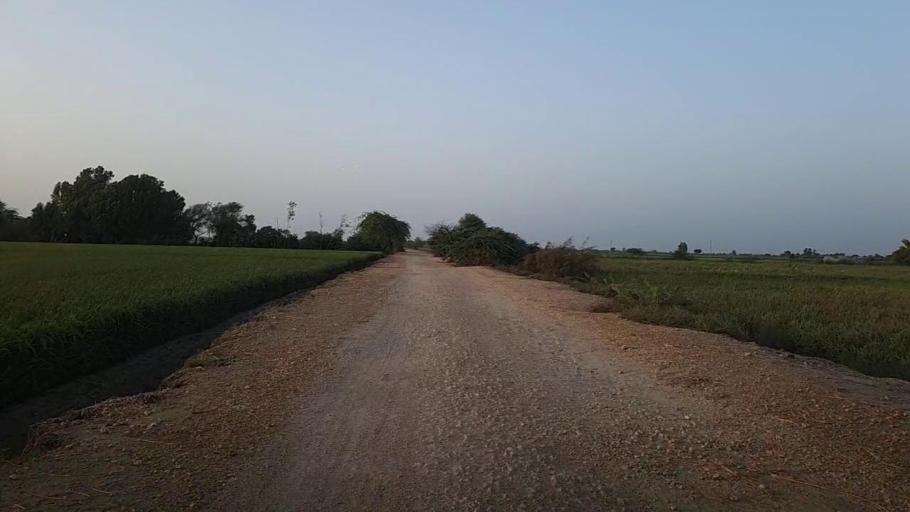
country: PK
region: Sindh
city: Kario
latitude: 24.7321
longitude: 68.4601
